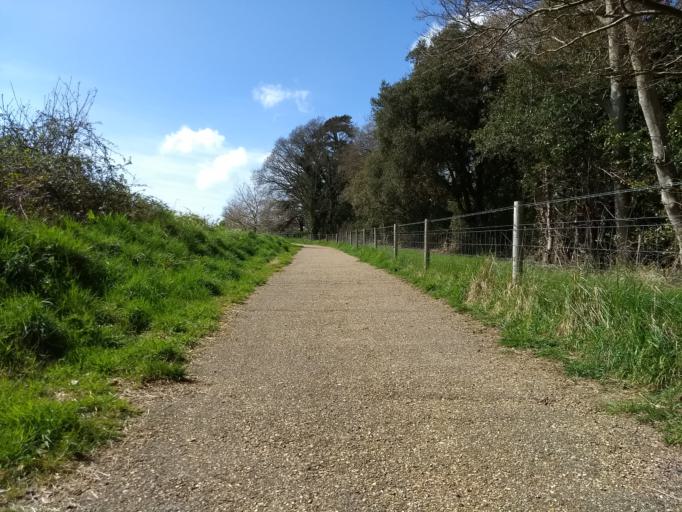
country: GB
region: England
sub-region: Isle of Wight
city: Newport
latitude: 50.7226
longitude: -1.2345
